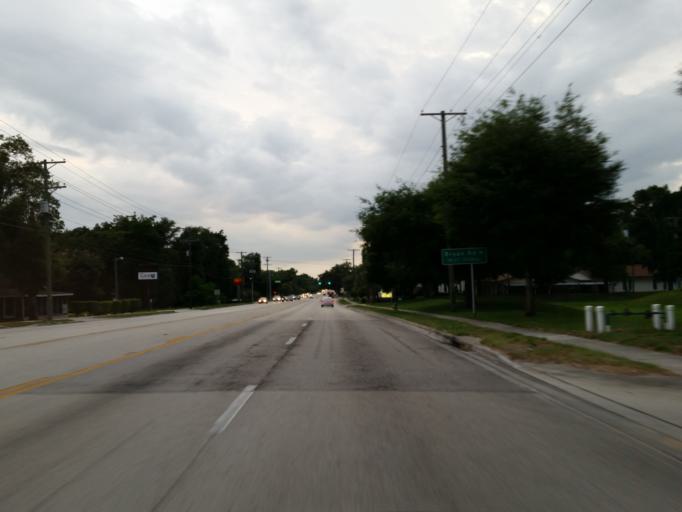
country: US
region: Florida
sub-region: Hillsborough County
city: Bloomingdale
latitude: 27.8938
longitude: -82.2748
